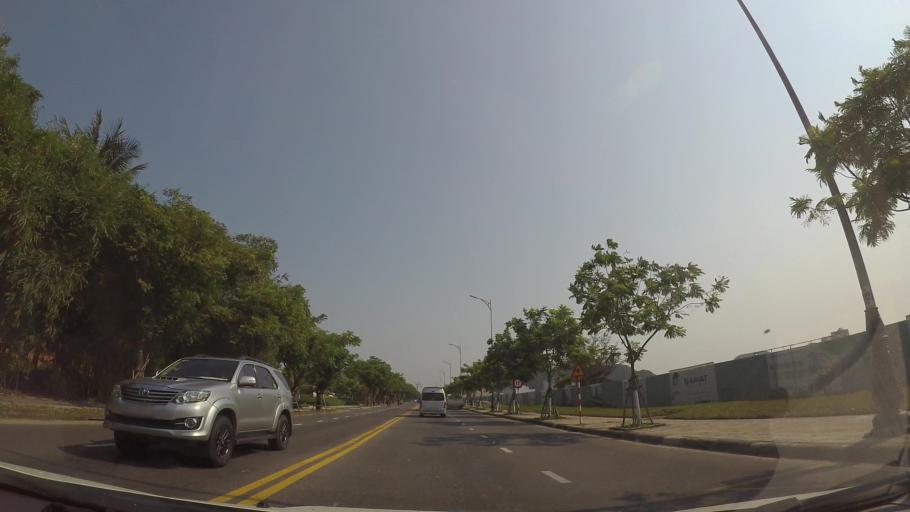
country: VN
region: Da Nang
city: Ngu Hanh Son
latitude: 16.0144
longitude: 108.2614
